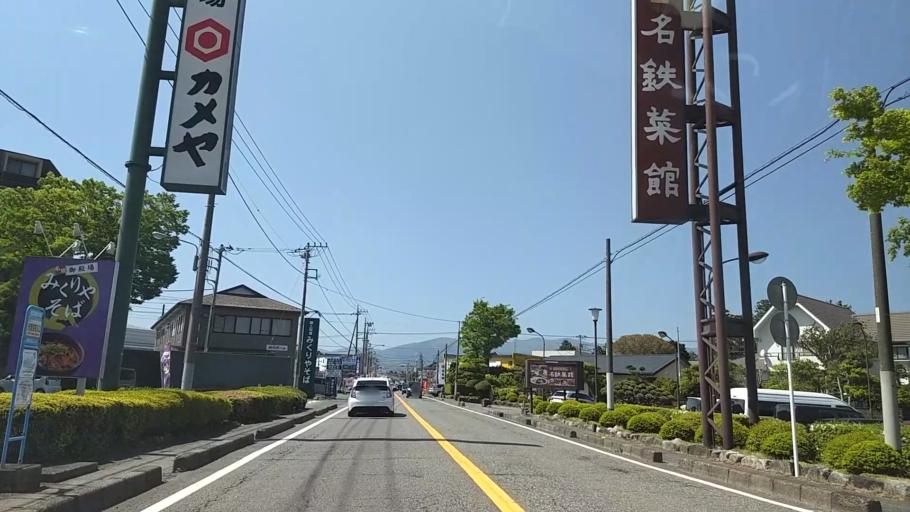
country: JP
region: Shizuoka
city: Gotemba
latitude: 35.2986
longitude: 138.9412
